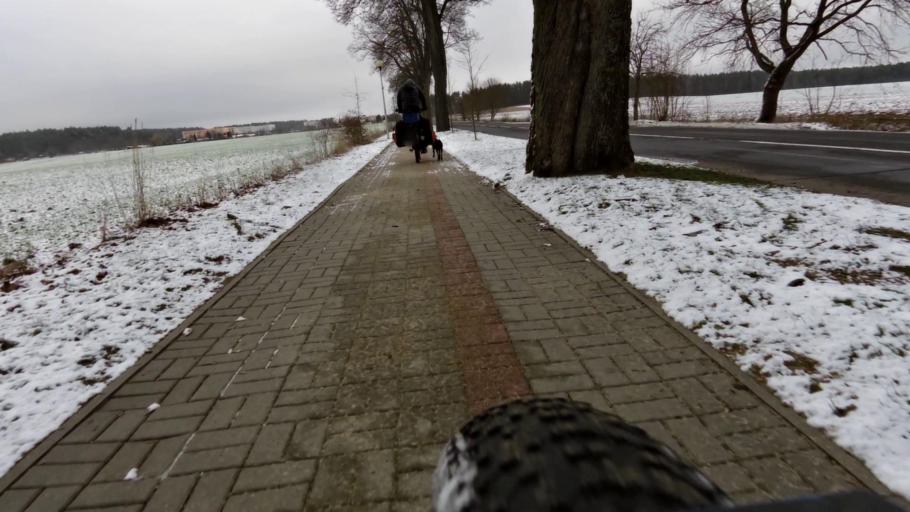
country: PL
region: West Pomeranian Voivodeship
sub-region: Powiat walecki
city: Miroslawiec
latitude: 53.3641
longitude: 16.0844
